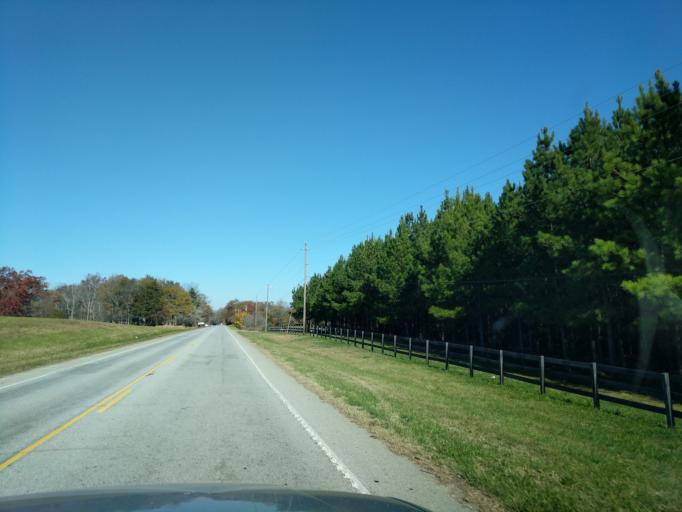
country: US
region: South Carolina
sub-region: Spartanburg County
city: Landrum
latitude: 35.0990
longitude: -82.2264
